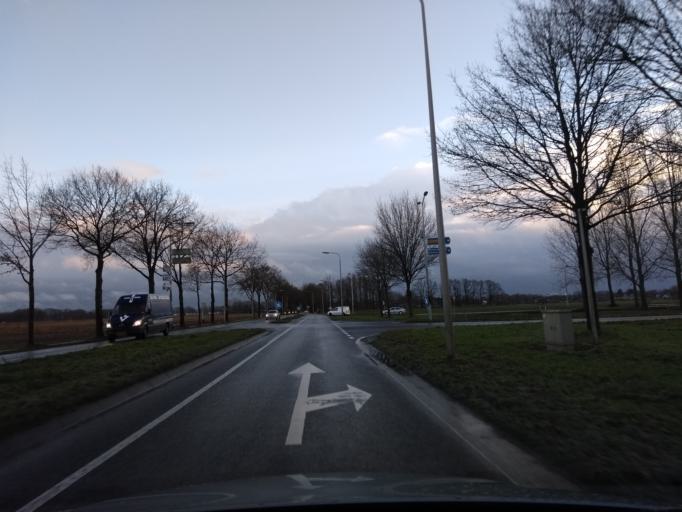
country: NL
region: Overijssel
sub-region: Gemeente Twenterand
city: Vriezenveen
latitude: 52.3885
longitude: 6.6219
